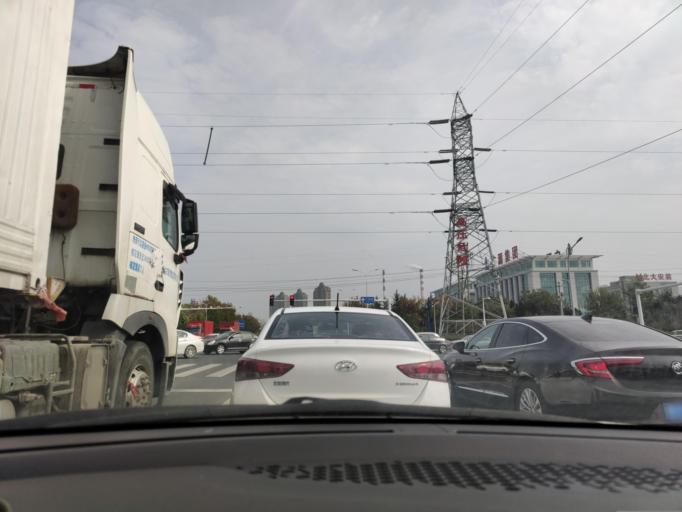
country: CN
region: Shandong Sheng
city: Zhichu
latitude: 37.5351
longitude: 121.2992
